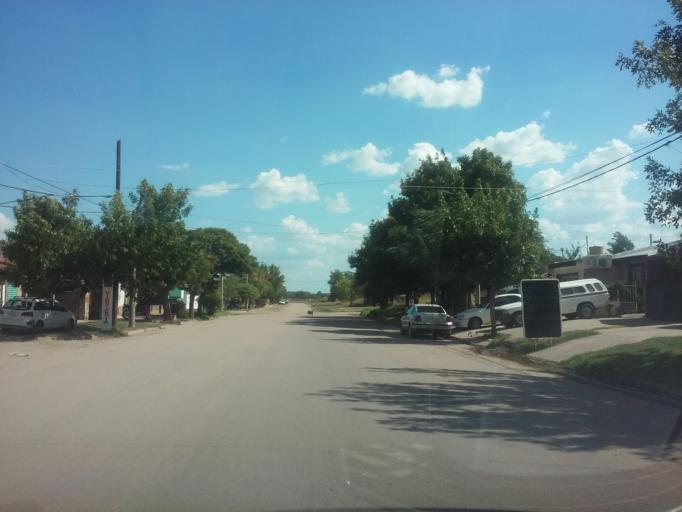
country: AR
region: La Pampa
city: Santa Rosa
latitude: -36.6451
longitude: -64.2961
